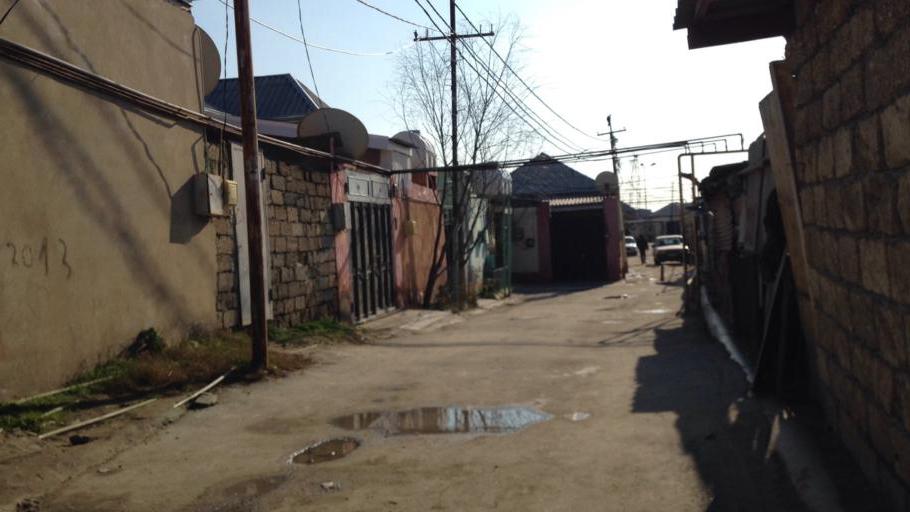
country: AZ
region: Baki
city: Sabuncu
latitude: 40.4478
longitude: 49.9328
